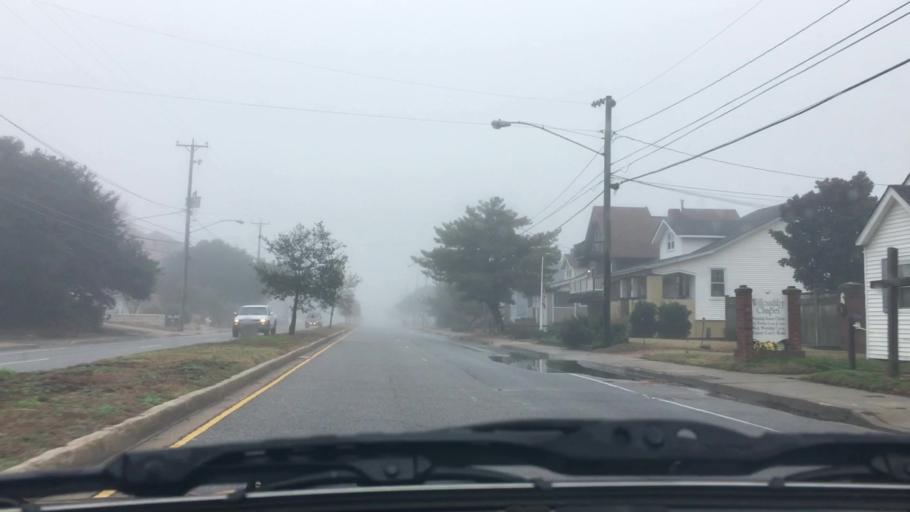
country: US
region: Virginia
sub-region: City of Hampton
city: East Hampton
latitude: 36.9650
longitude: -76.2716
